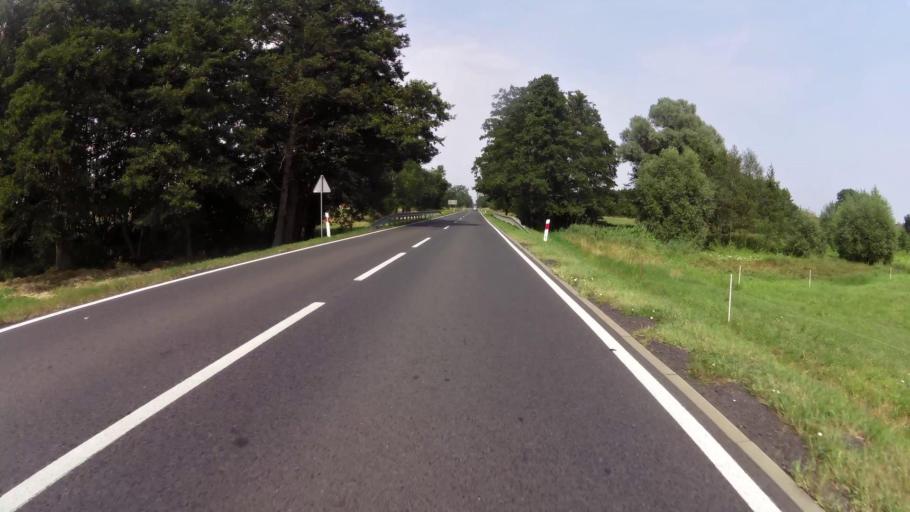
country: PL
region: West Pomeranian Voivodeship
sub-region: Powiat gryfinski
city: Mieszkowice
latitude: 52.8267
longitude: 14.4952
